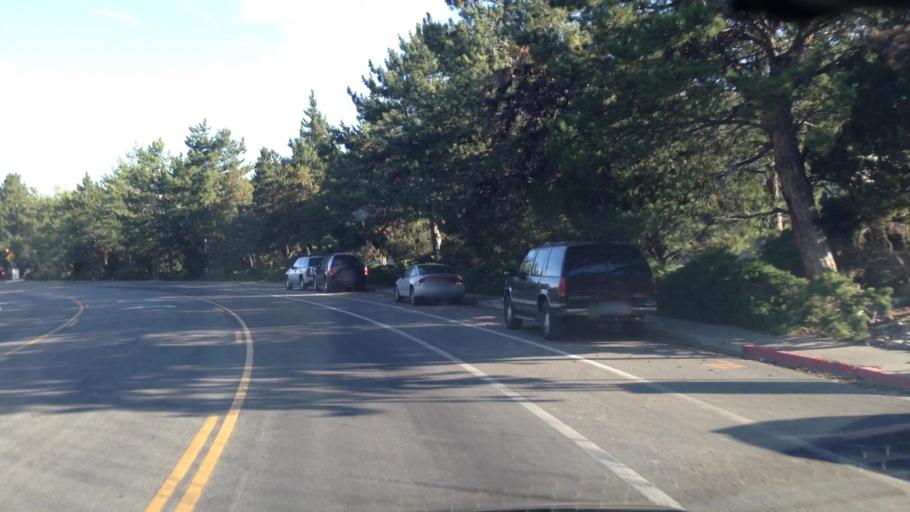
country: US
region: Nevada
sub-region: Washoe County
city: Reno
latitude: 39.4788
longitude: -119.8125
